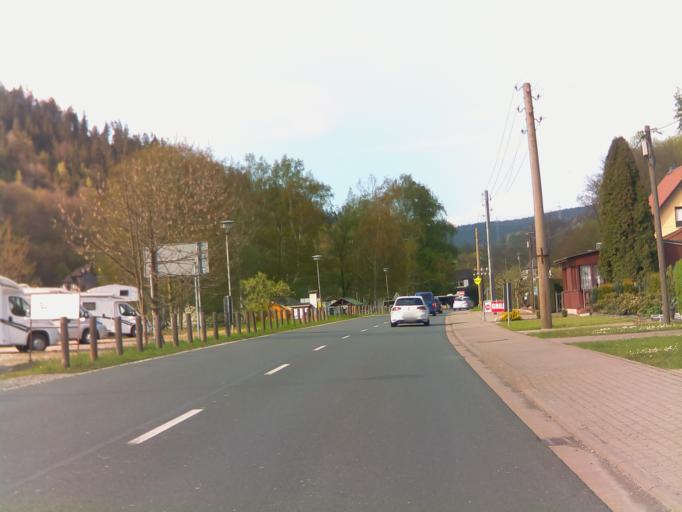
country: DE
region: Thuringia
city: Kaulsdorf
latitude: 50.5952
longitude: 11.4339
